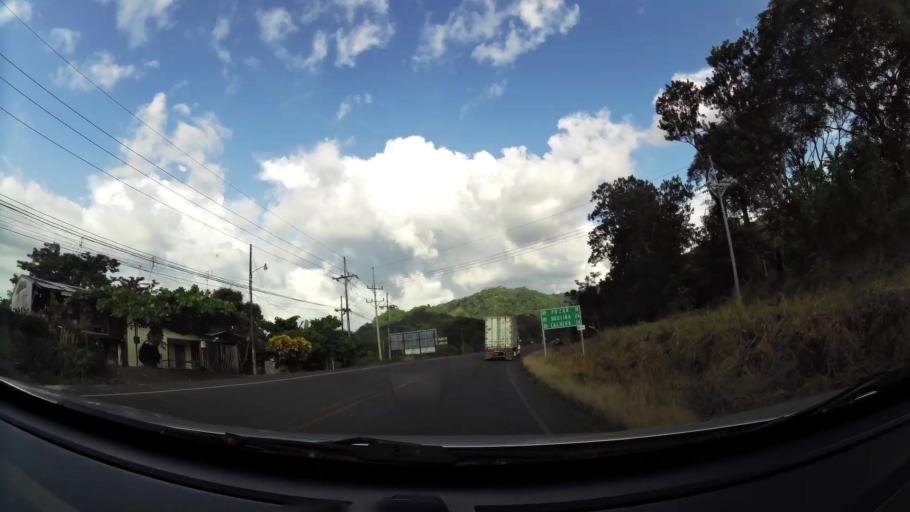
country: CR
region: Puntarenas
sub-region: Canton de Garabito
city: Jaco
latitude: 9.7553
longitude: -84.6231
